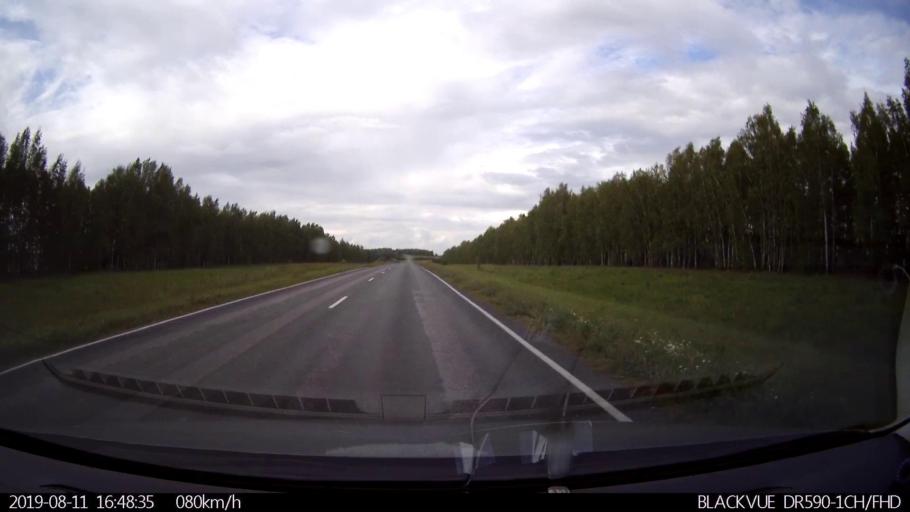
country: RU
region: Ulyanovsk
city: Mayna
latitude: 54.2093
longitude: 47.6924
